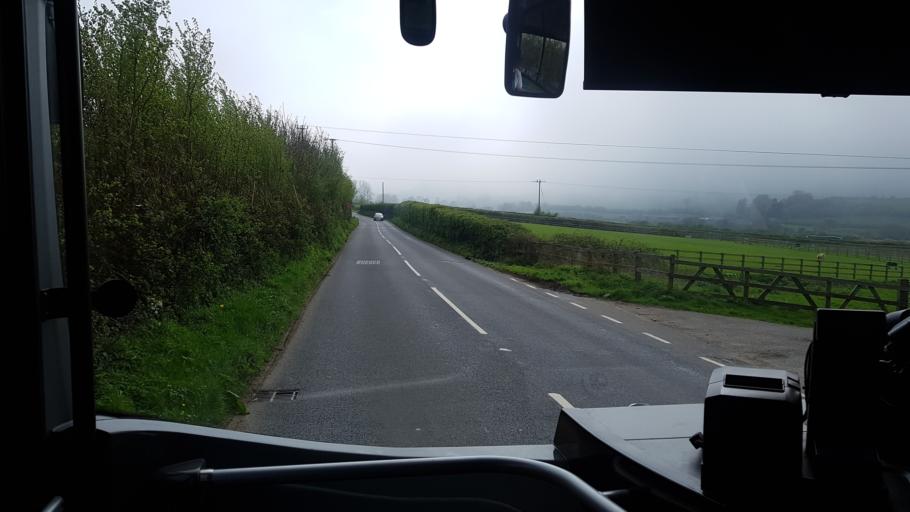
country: GB
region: England
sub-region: Isle of Wight
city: Ventnor
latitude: 50.6284
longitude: -1.2224
